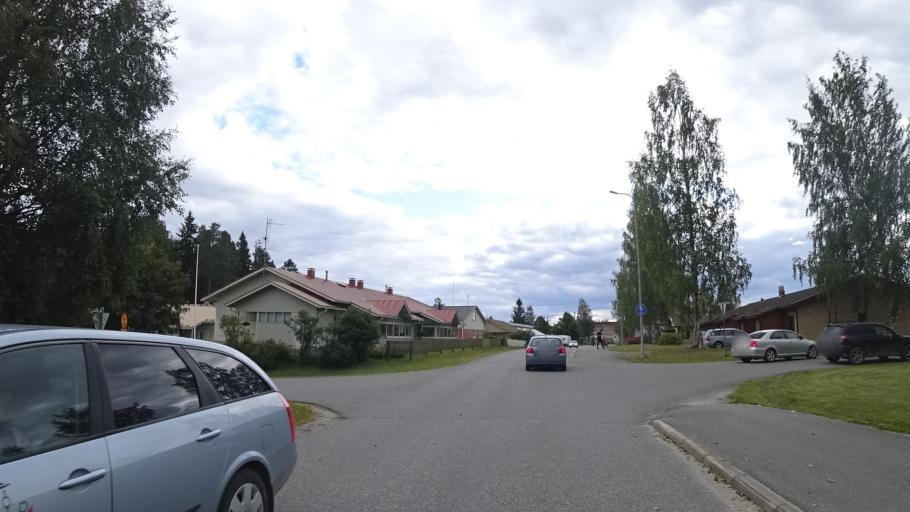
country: FI
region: North Karelia
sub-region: Joensuu
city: Ilomantsi
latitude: 62.6713
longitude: 30.9370
